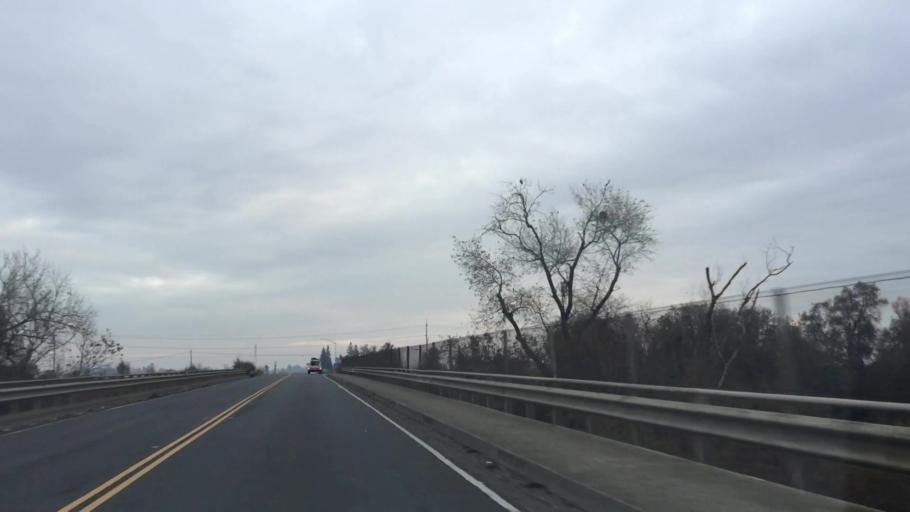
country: US
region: California
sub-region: Yuba County
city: Marysville
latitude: 39.1676
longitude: -121.5903
